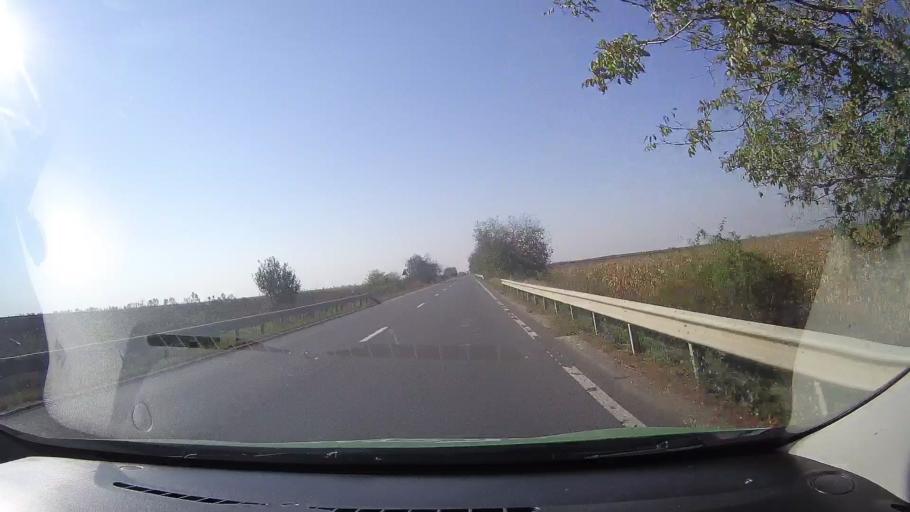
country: RO
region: Satu Mare
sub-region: Comuna Petresti
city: Petresti
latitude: 47.6280
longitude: 22.3901
